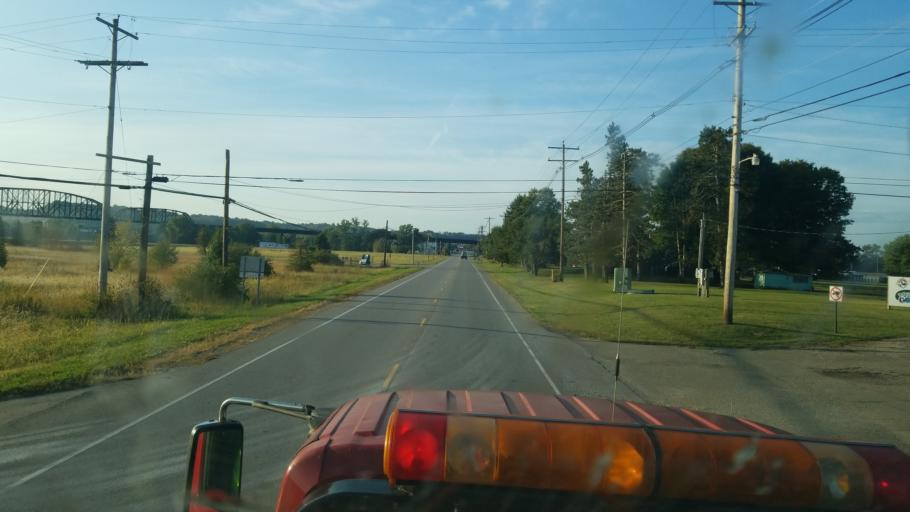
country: US
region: West Virginia
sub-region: Mason County
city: Point Pleasant
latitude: 38.8512
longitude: -82.1450
